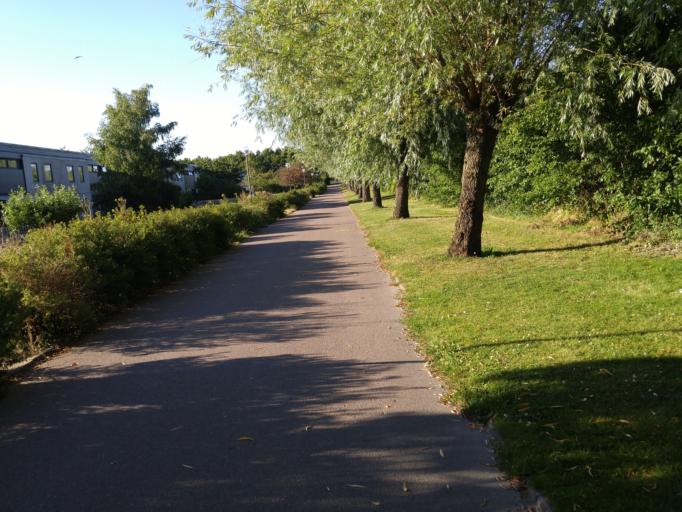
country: SE
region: Skane
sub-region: Lunds Kommun
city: Lund
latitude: 55.7262
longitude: 13.2019
